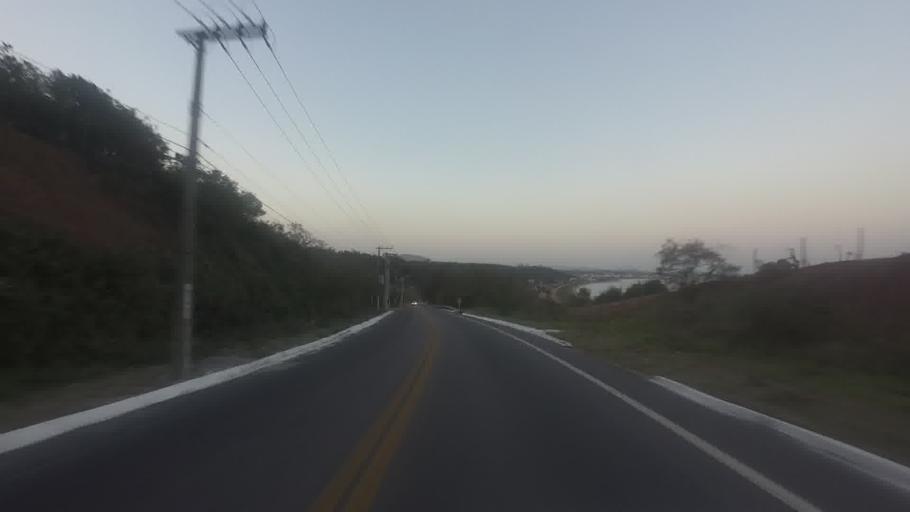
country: BR
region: Espirito Santo
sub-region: Piuma
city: Piuma
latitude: -20.8678
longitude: -40.7608
